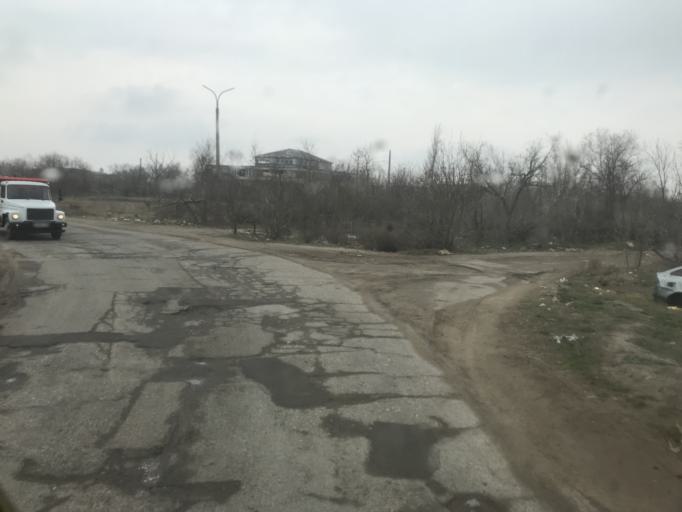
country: RU
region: Volgograd
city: Krasnoslobodsk
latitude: 48.5361
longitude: 44.6091
